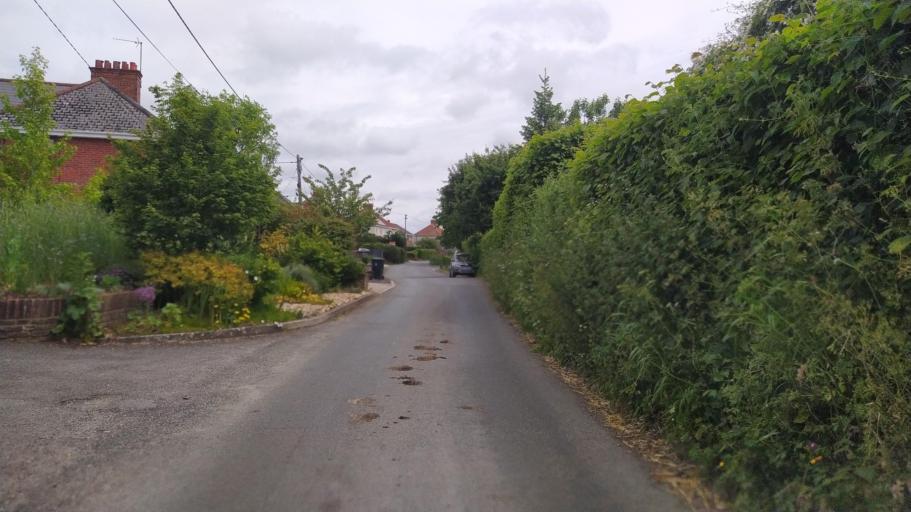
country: GB
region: England
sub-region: Dorset
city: Sturminster Newton
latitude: 50.8989
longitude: -2.2824
